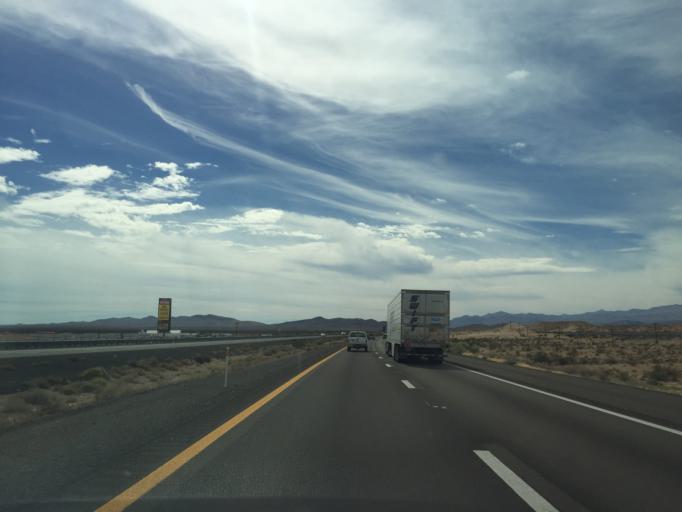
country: US
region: Nevada
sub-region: Clark County
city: Moapa Town
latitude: 36.5065
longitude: -114.7540
